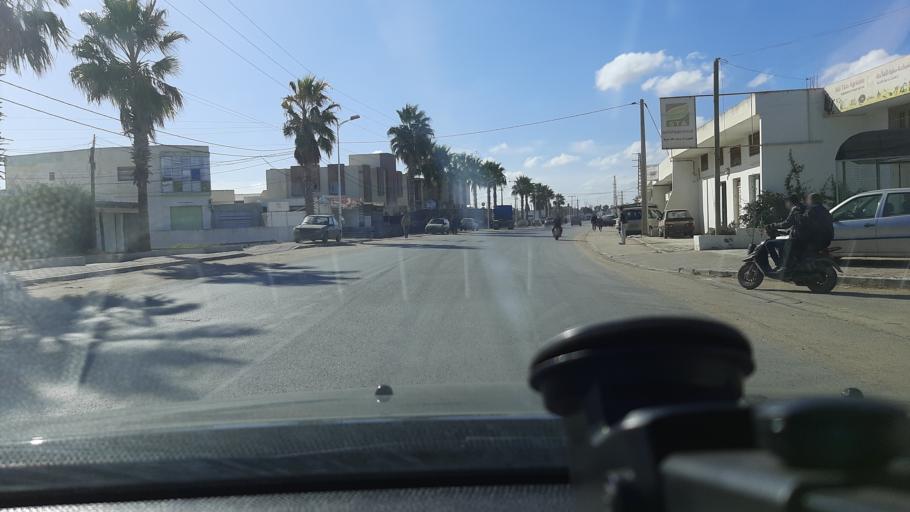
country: TN
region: Safaqis
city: Sfax
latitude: 34.8088
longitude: 10.7062
